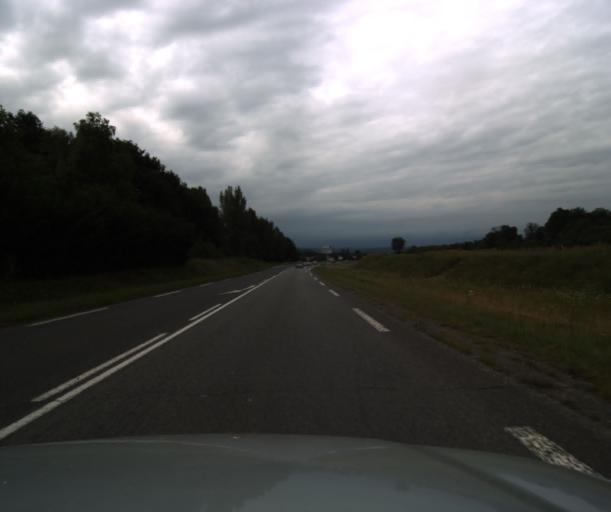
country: FR
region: Midi-Pyrenees
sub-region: Departement des Hautes-Pyrenees
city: Juillan
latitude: 43.1958
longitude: 0.0092
